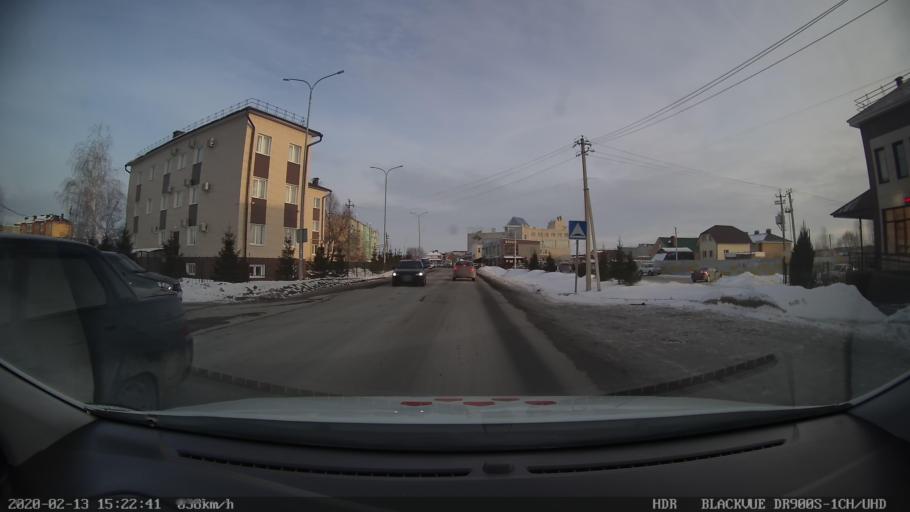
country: RU
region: Tatarstan
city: Vysokaya Gora
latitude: 55.9201
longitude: 49.3106
